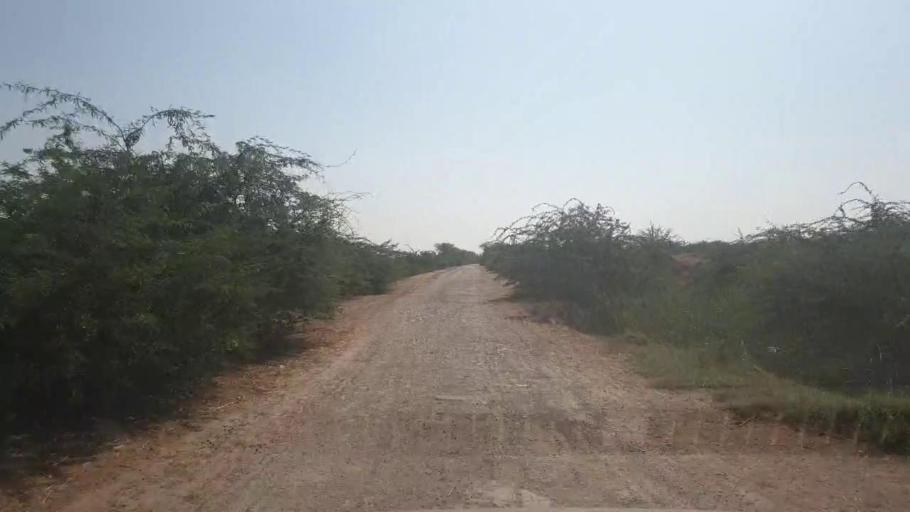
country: PK
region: Sindh
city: Badin
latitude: 24.5867
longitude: 68.8458
